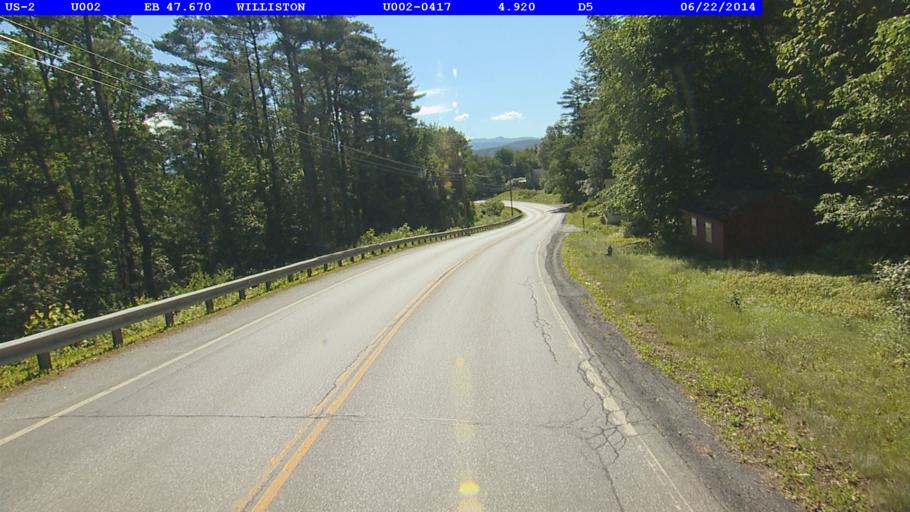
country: US
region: Vermont
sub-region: Chittenden County
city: Williston
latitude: 44.4344
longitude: -73.0450
